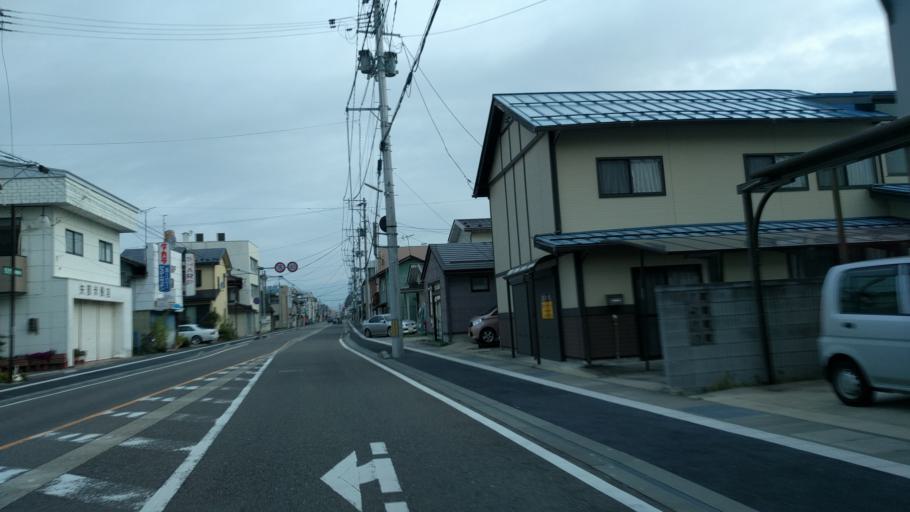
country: JP
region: Fukushima
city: Kitakata
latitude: 37.6474
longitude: 139.8686
